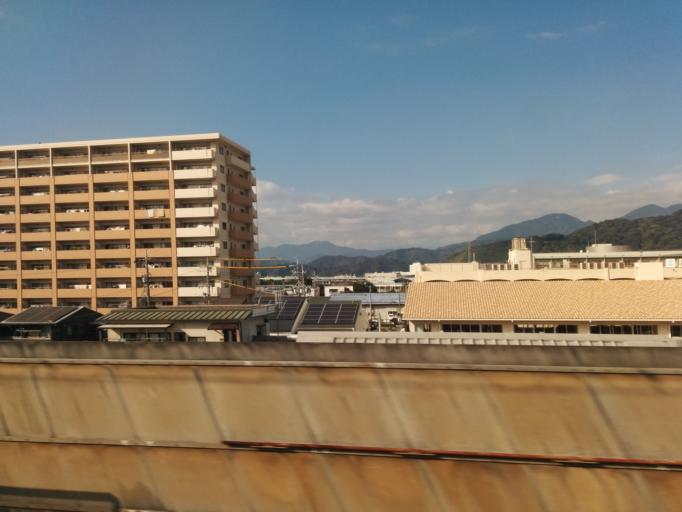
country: JP
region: Shizuoka
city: Shizuoka-shi
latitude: 35.0018
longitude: 138.4398
